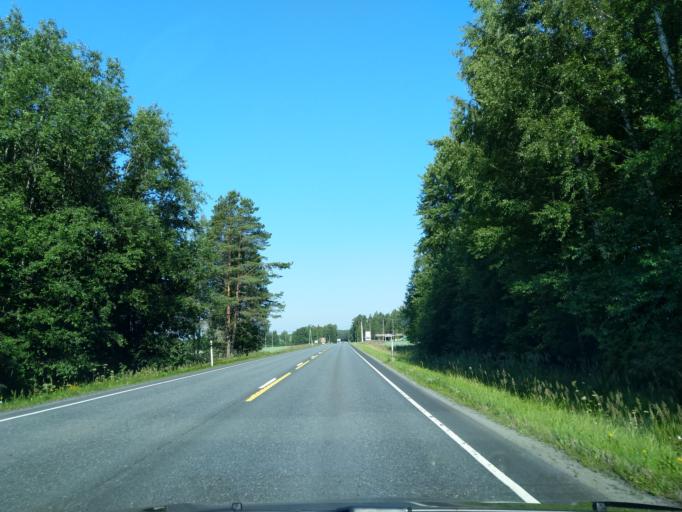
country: FI
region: Haeme
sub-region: Forssa
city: Humppila
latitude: 60.9678
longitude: 23.2857
